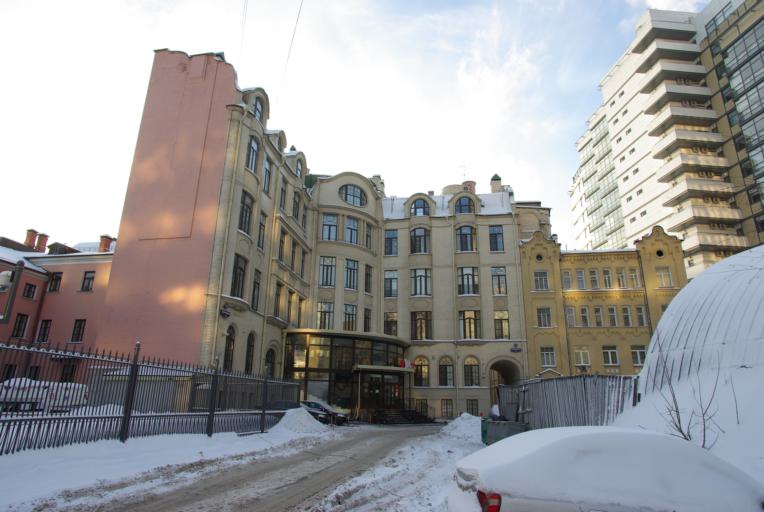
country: RU
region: Moscow
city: Moscow
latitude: 55.7687
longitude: 37.6434
